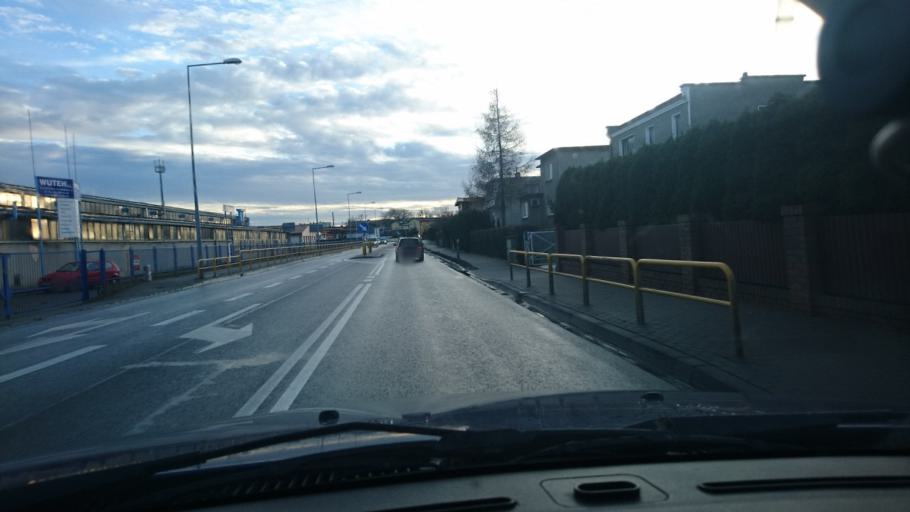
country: PL
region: Greater Poland Voivodeship
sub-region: Powiat kepinski
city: Kepno
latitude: 51.2776
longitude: 17.9906
